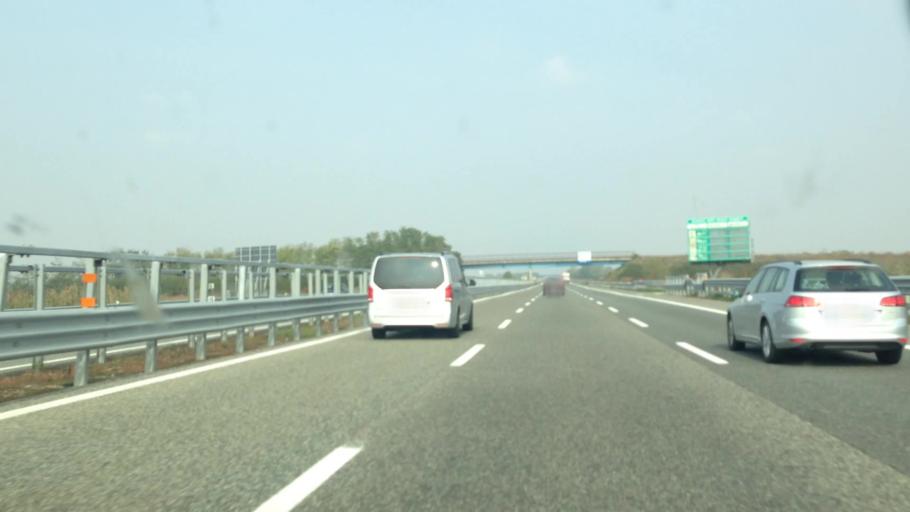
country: IT
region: Piedmont
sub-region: Provincia di Vercelli
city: Caresana
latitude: 45.2097
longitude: 8.4850
